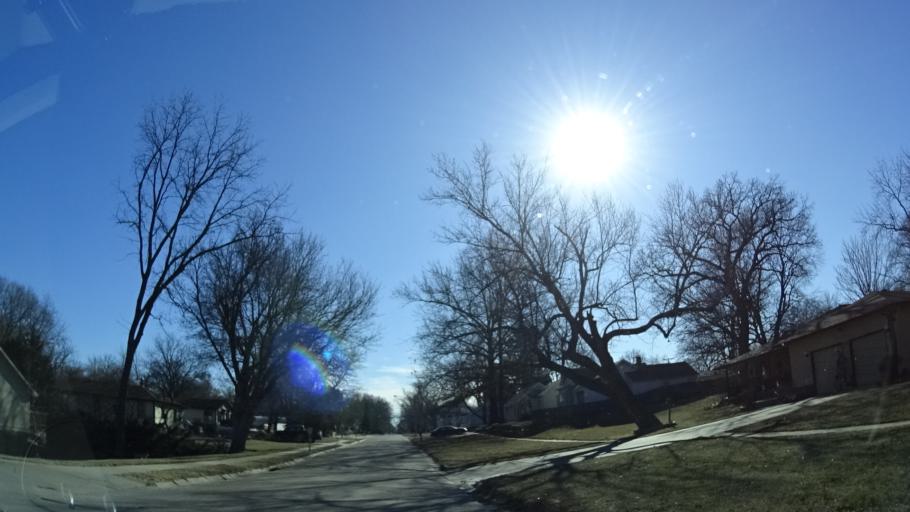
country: US
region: Nebraska
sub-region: Sarpy County
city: Bellevue
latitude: 41.1427
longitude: -95.8909
